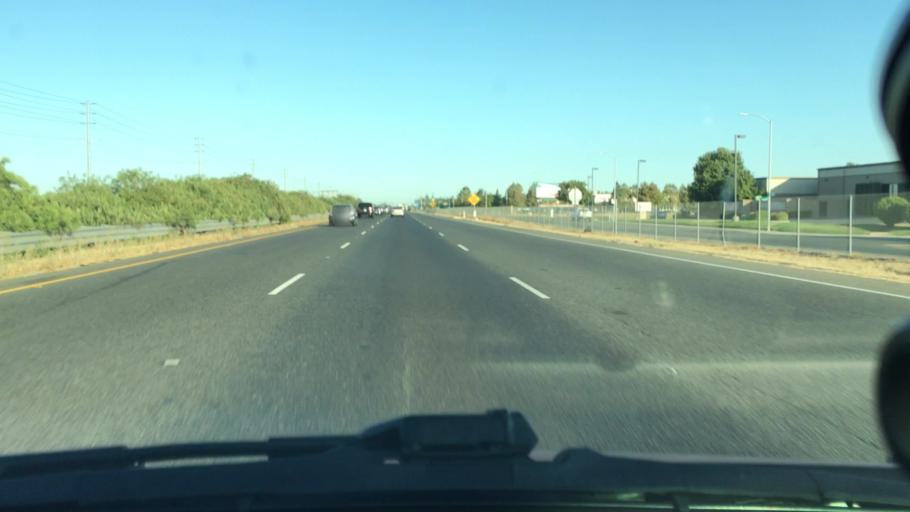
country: US
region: California
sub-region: Sacramento County
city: Elk Grove
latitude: 38.3806
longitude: -121.3660
